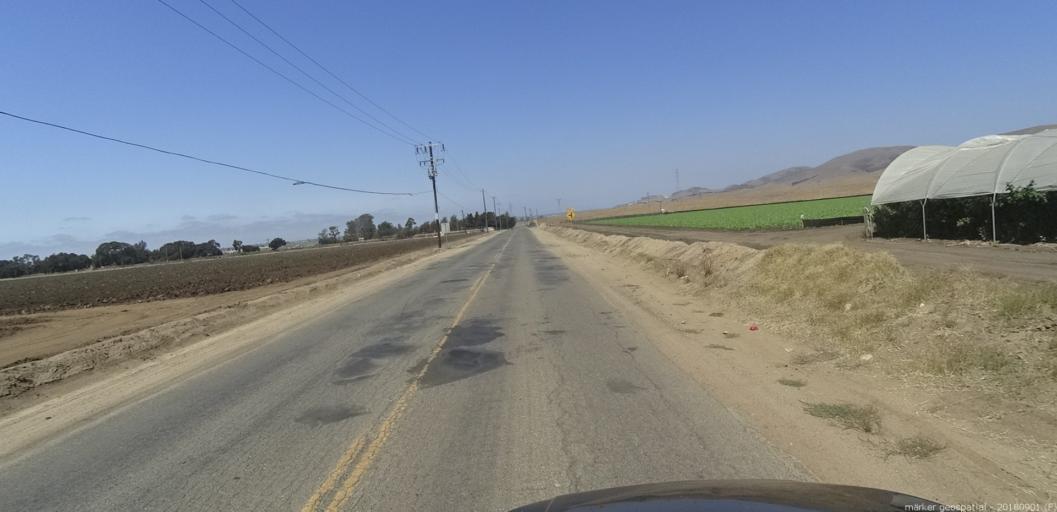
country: US
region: California
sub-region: Monterey County
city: Salinas
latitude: 36.6966
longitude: -121.5725
